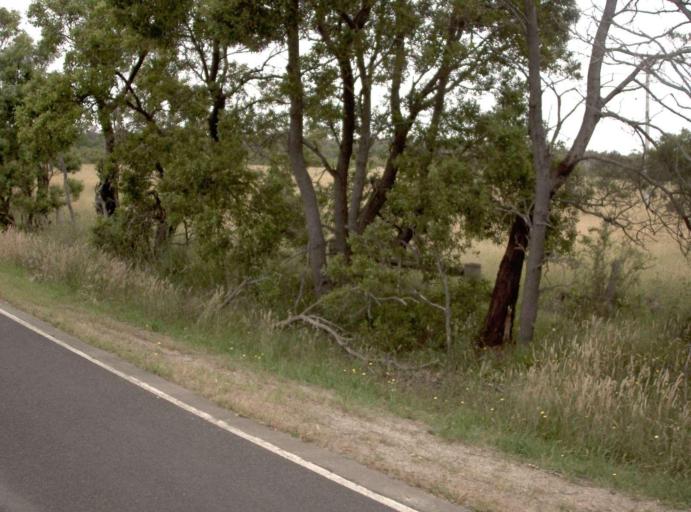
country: AU
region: Victoria
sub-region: Latrobe
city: Traralgon
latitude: -38.4909
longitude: 146.8192
